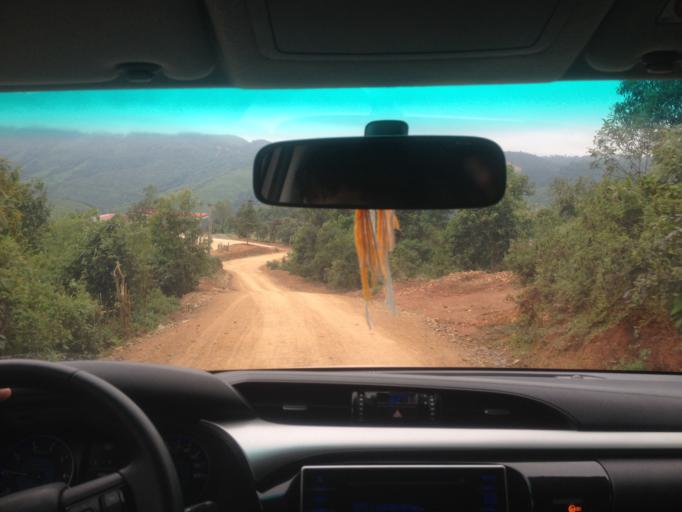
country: TH
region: Nan
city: Chaloem Phra Kiat
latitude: 19.9965
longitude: 101.1335
